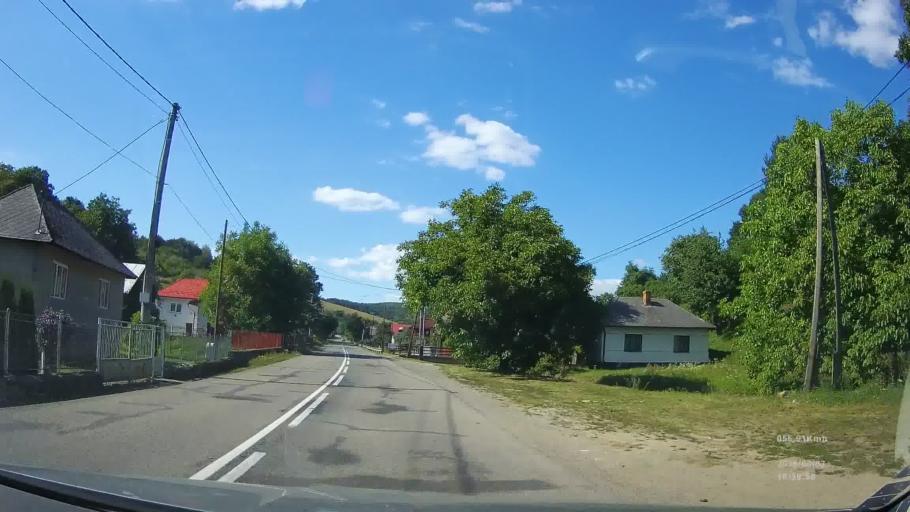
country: SK
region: Presovsky
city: Giraltovce
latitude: 49.1147
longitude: 21.6068
